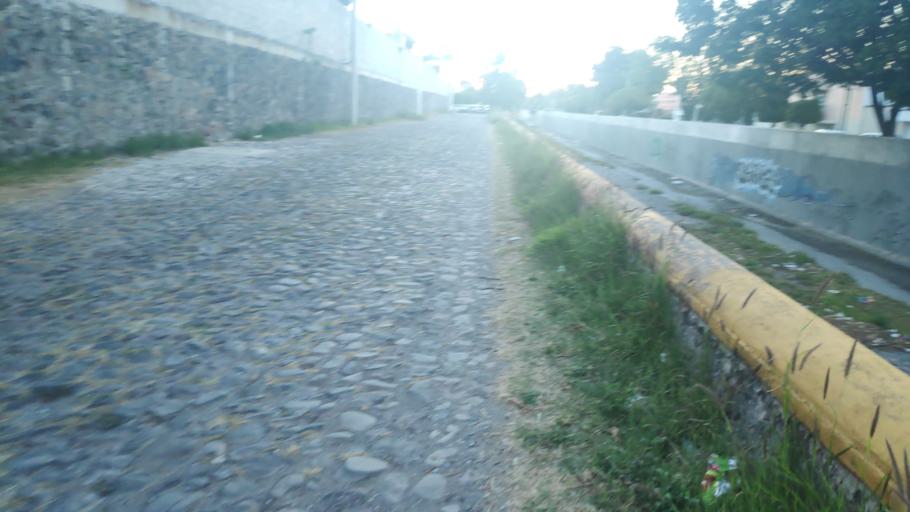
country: MX
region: Queretaro
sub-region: Queretaro
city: Santiago de Queretaro
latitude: 20.5799
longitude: -100.3778
